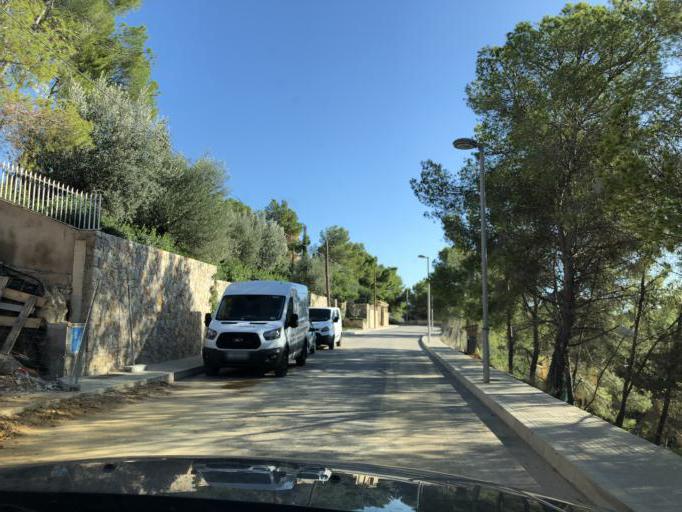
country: ES
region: Balearic Islands
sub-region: Illes Balears
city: Camp de Mar
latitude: 39.5408
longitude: 2.4100
